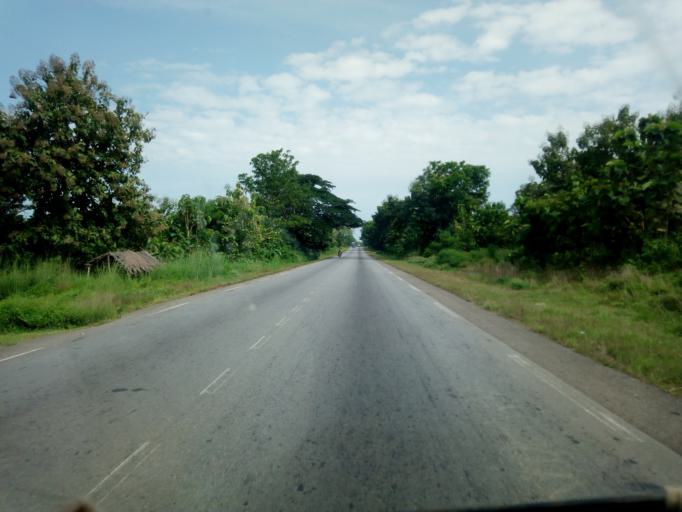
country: TG
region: Plateaux
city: Notse
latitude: 7.0489
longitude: 1.1556
